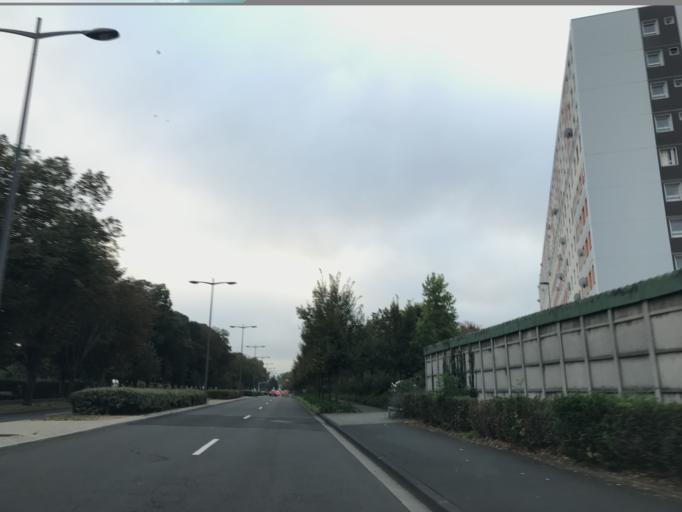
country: FR
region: Auvergne
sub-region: Departement du Puy-de-Dome
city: Gerzat
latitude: 45.8023
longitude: 3.1202
